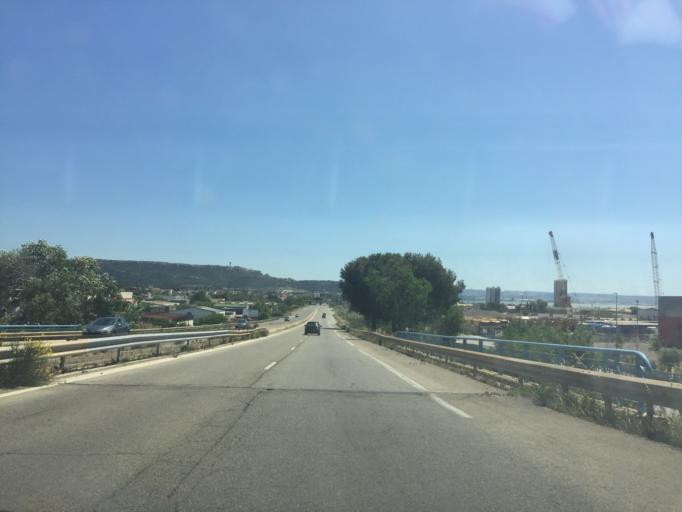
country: FR
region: Provence-Alpes-Cote d'Azur
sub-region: Departement des Bouches-du-Rhone
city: Rognac
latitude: 43.5005
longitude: 5.2124
